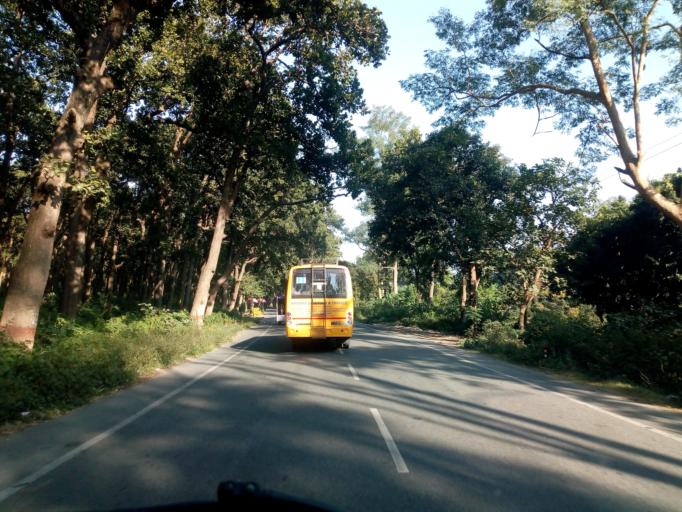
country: IN
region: Uttarakhand
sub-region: Dehradun
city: Dehradun
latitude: 30.3471
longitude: 77.8790
